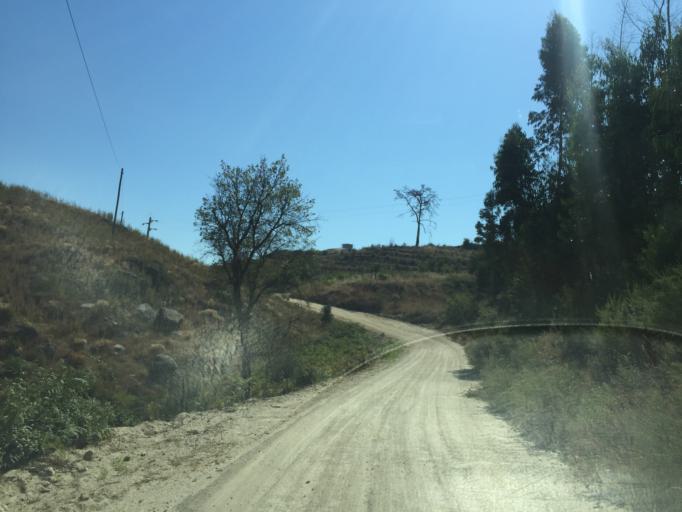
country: PT
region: Santarem
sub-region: Constancia
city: Constancia
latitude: 39.5419
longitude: -8.2785
